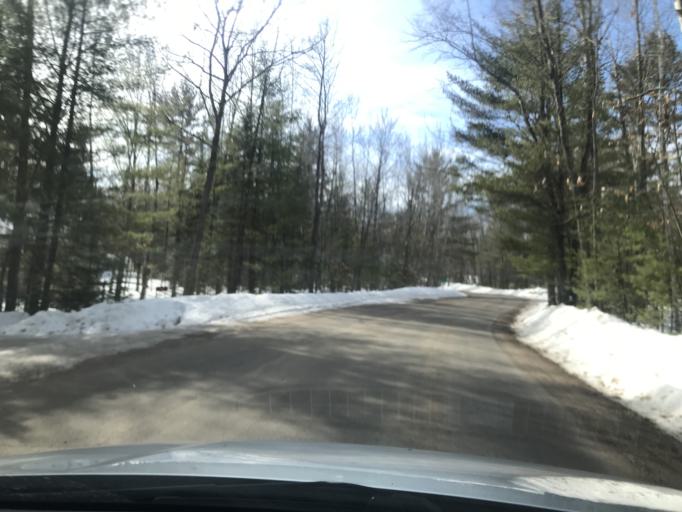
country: US
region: Wisconsin
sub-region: Menominee County
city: Legend Lake
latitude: 45.1171
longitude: -88.4332
